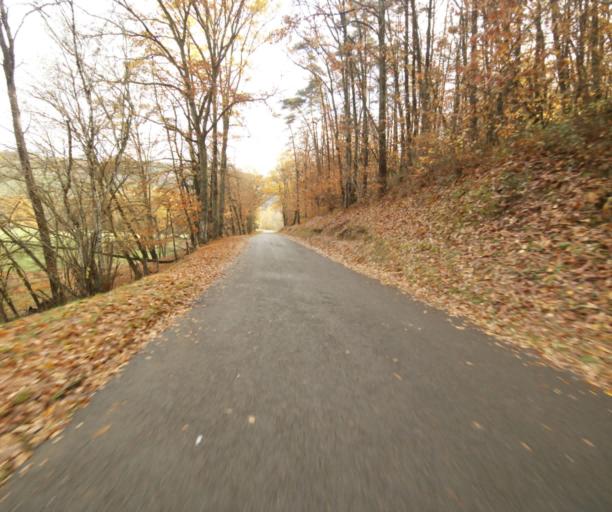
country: FR
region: Limousin
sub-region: Departement de la Correze
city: Saint-Mexant
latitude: 45.2359
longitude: 1.6386
